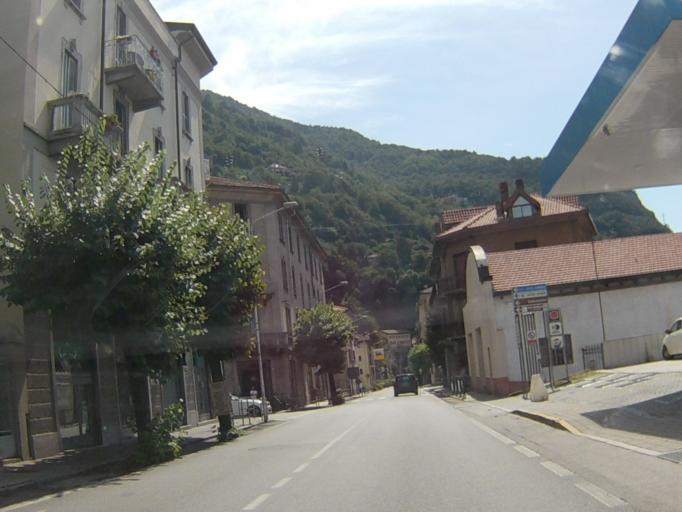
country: IT
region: Lombardy
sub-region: Provincia di Lecco
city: Bellano
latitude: 46.0415
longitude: 9.3022
